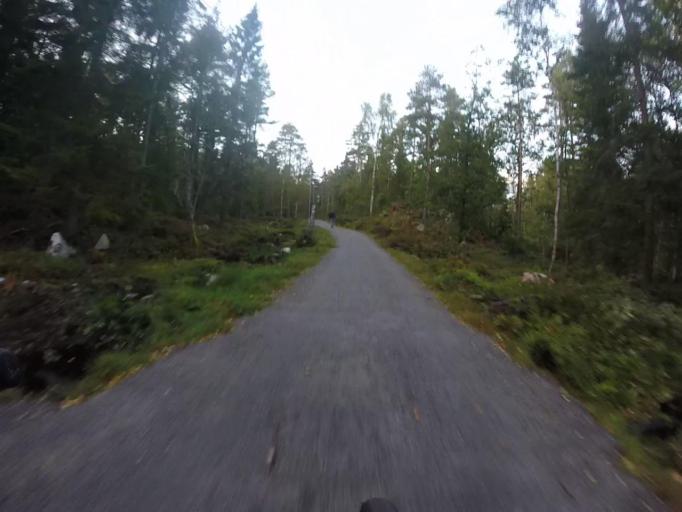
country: SE
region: Vaestra Goetaland
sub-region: Trollhattan
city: Trollhattan
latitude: 58.2945
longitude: 12.2697
